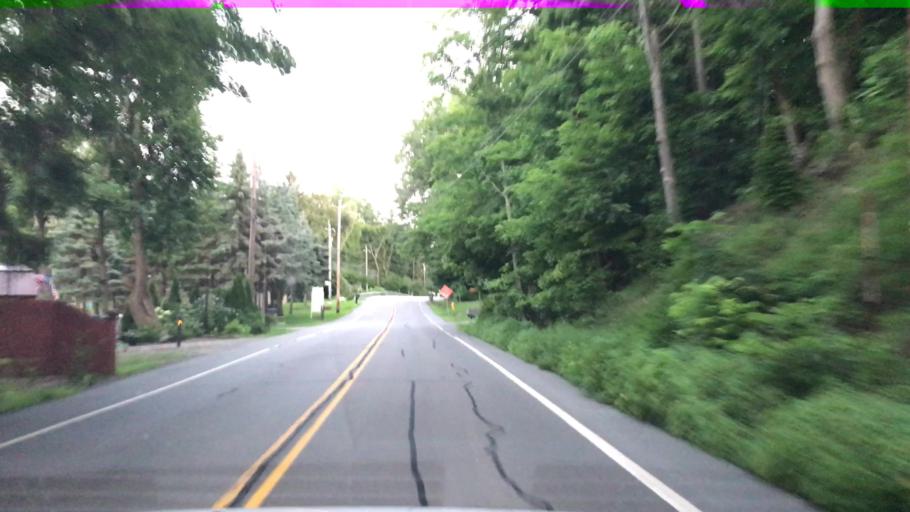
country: US
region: New York
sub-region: Steuben County
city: Sylvan Beach
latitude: 42.5324
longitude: -77.1531
